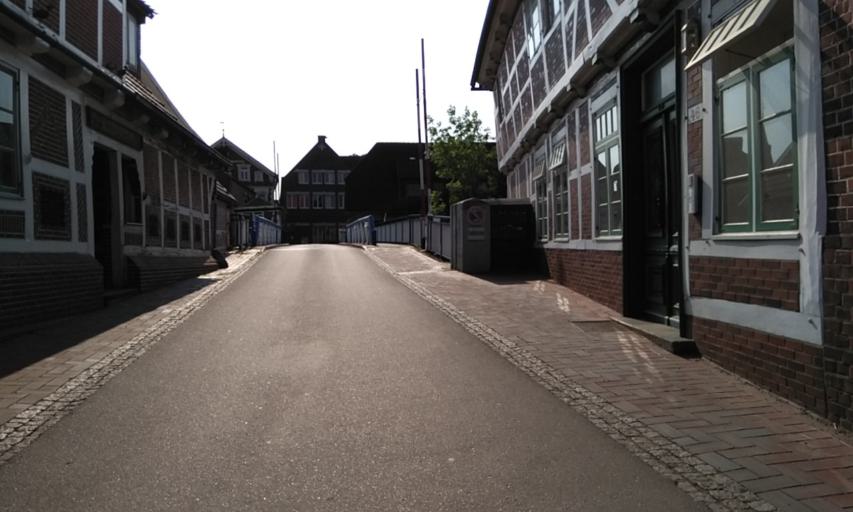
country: DE
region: Lower Saxony
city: Jork
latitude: 53.5108
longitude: 9.7313
